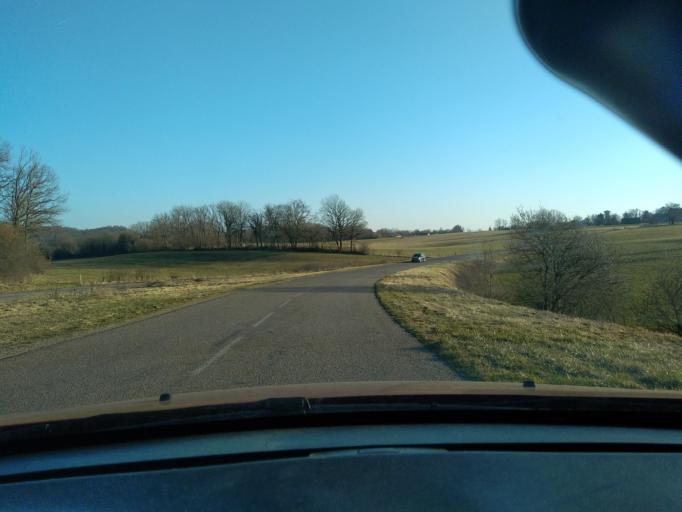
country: FR
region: Franche-Comte
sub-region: Departement du Jura
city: Perrigny
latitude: 46.6403
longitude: 5.6457
